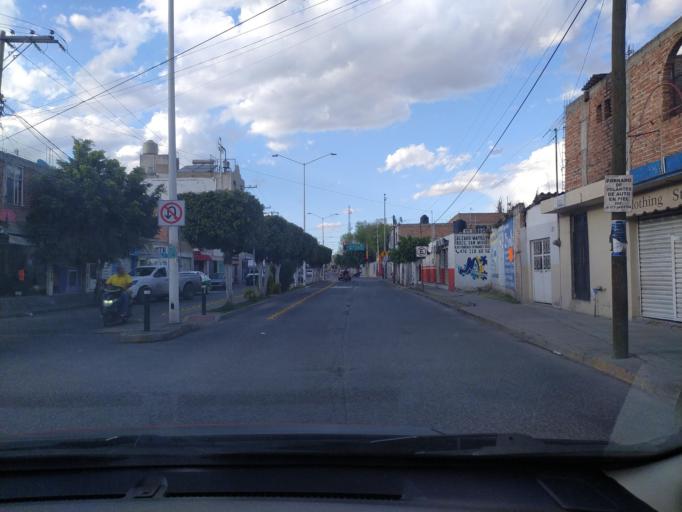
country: LA
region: Oudomxai
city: Muang La
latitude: 21.0157
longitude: 101.8500
